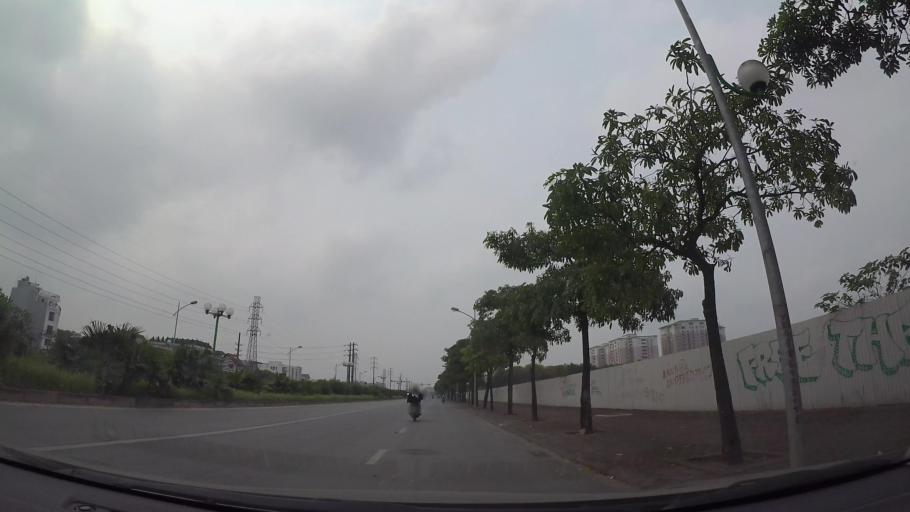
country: VN
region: Ha Noi
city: Trau Quy
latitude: 21.0540
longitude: 105.9062
